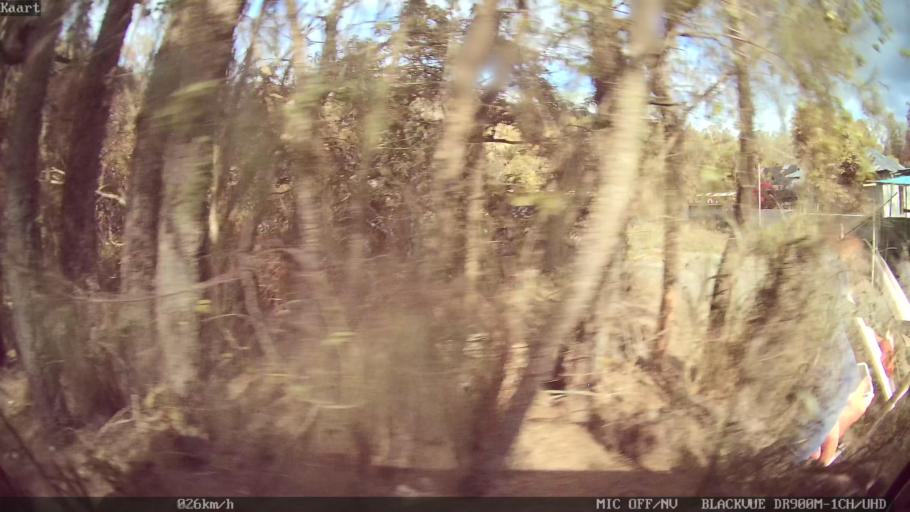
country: ID
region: Bali
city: Banjar Kedisan
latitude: -8.2299
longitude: 115.3582
